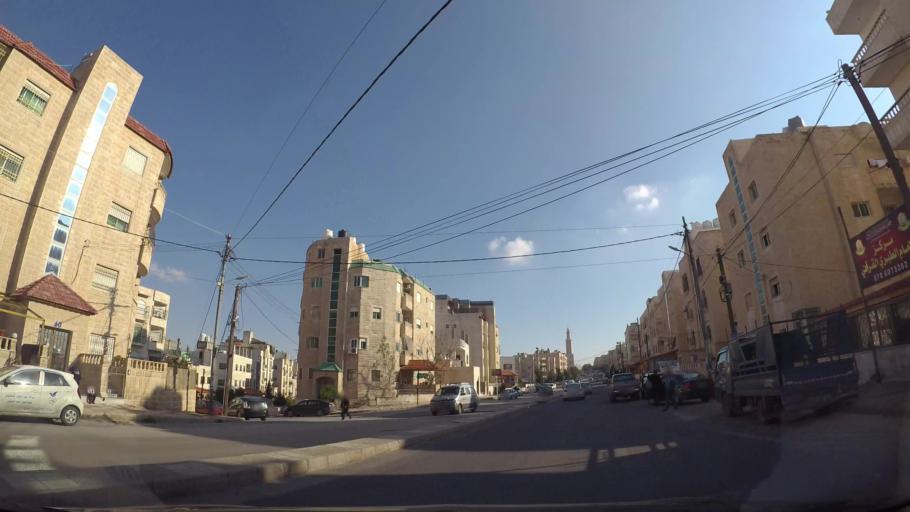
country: JO
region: Amman
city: Amman
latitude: 31.9827
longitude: 35.9460
